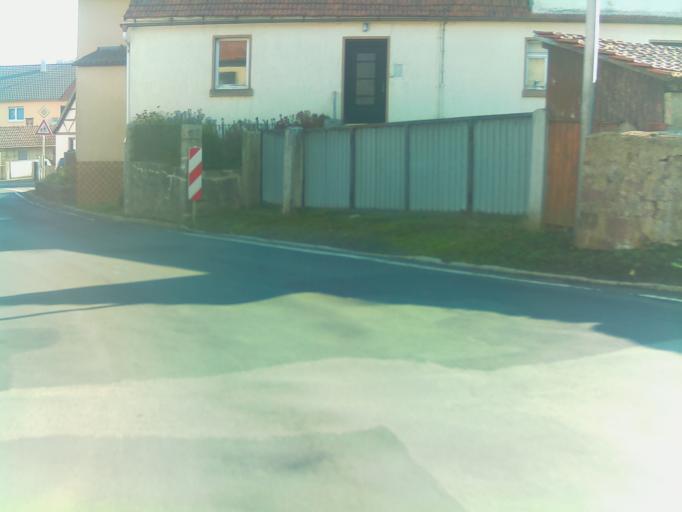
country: DE
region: Bavaria
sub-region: Regierungsbezirk Unterfranken
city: Niederlauer
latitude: 50.2963
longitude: 10.1283
